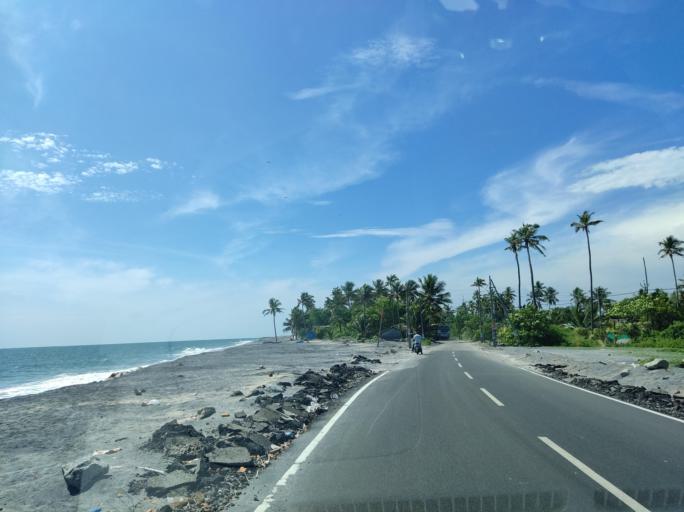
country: IN
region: Kerala
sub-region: Alappuzha
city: Kayankulam
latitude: 9.1671
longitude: 76.4493
